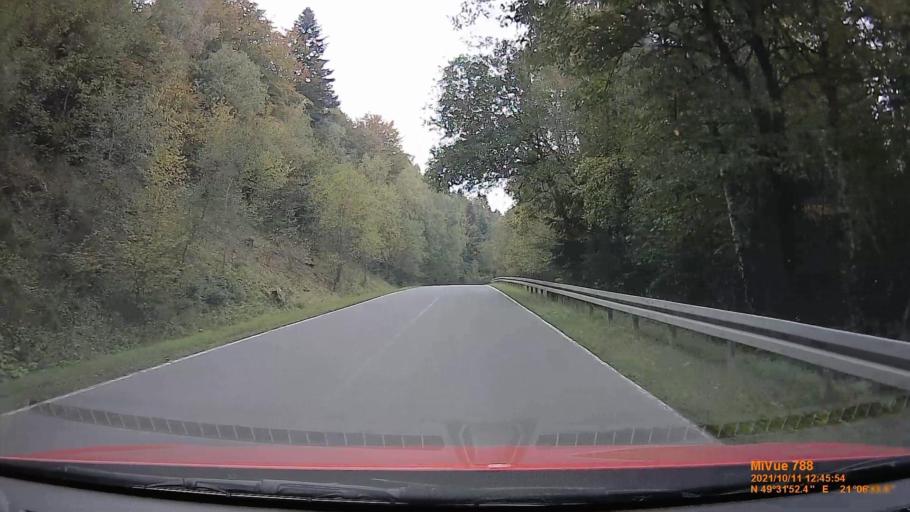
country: PL
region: Lesser Poland Voivodeship
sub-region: Powiat gorlicki
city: Uscie Gorlickie
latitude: 49.5313
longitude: 21.1091
